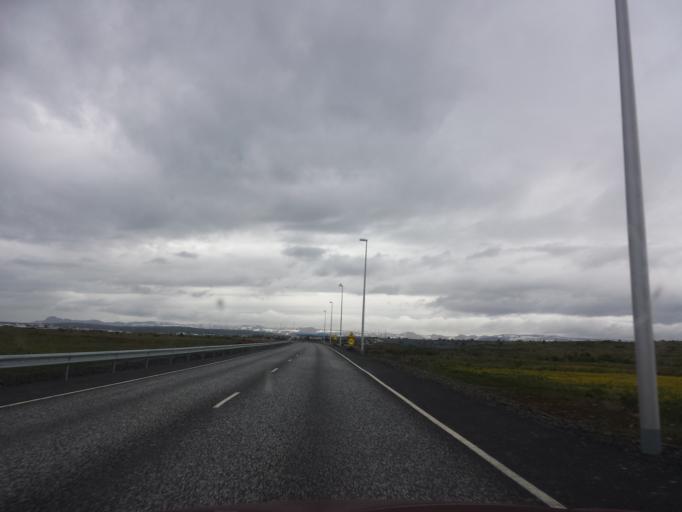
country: IS
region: Capital Region
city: Alftanes
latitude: 64.0934
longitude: -21.9934
